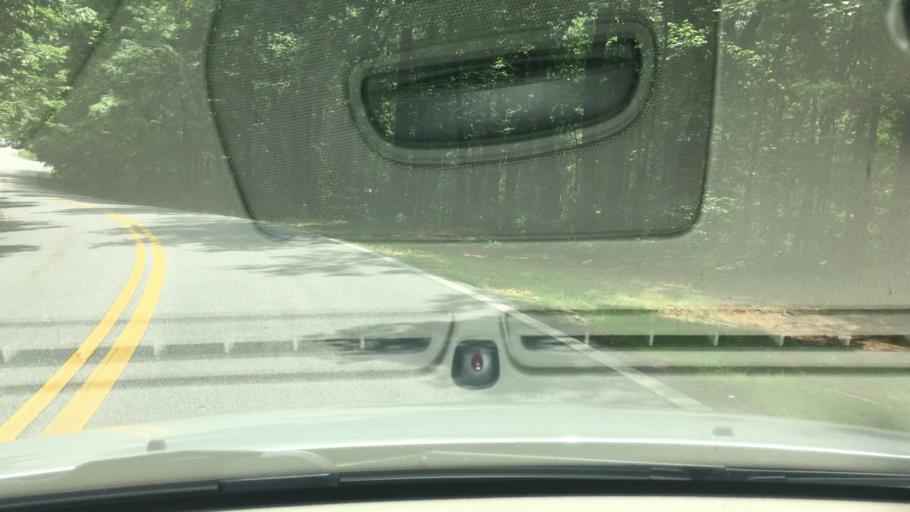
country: US
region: Georgia
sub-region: Dawson County
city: Dawsonville
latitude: 34.5581
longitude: -84.2519
